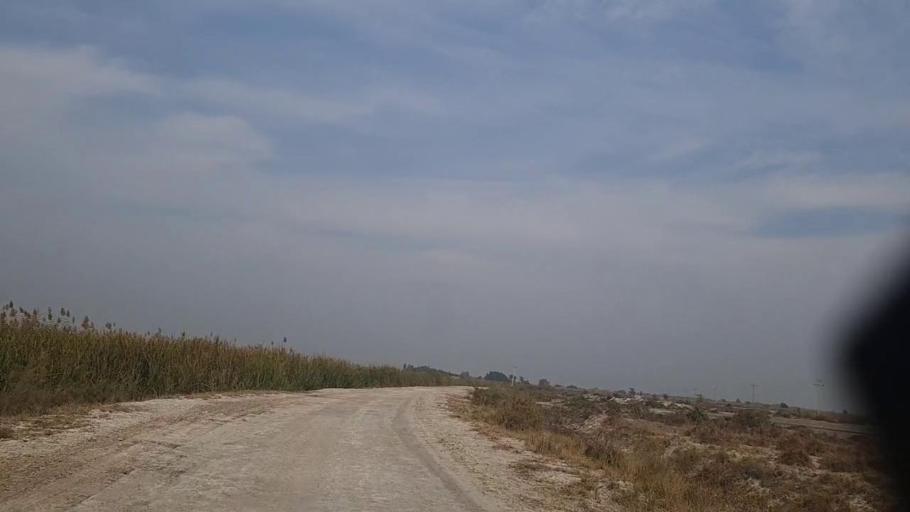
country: PK
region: Sindh
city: Daur
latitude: 26.3684
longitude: 68.2395
